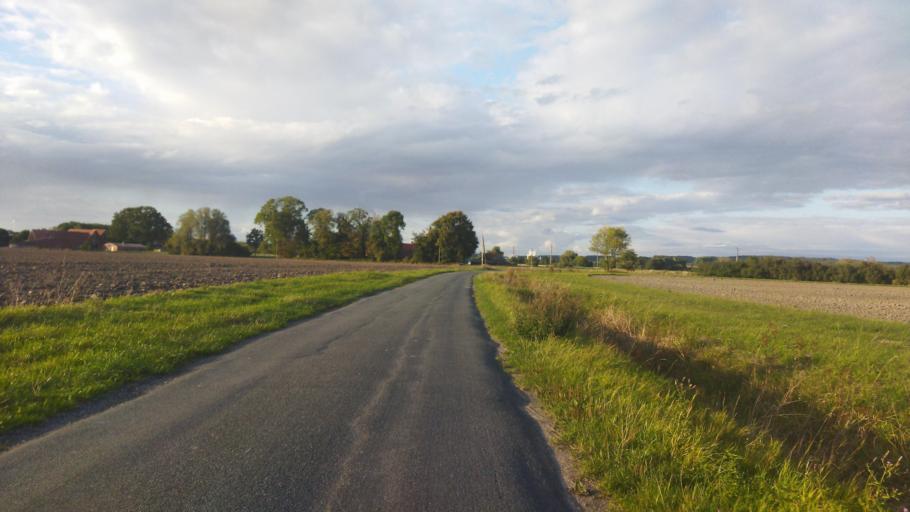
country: DE
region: North Rhine-Westphalia
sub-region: Regierungsbezirk Munster
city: Billerbeck
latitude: 51.9638
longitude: 7.2595
